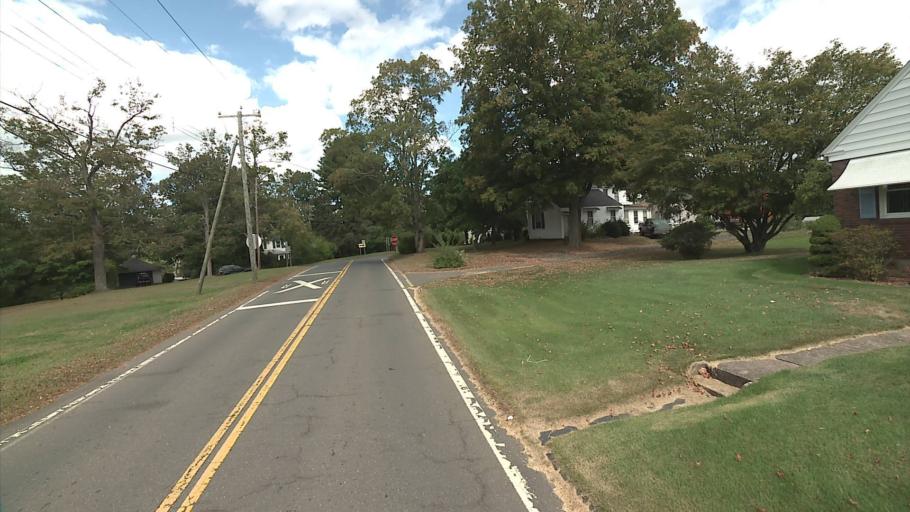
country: US
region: Connecticut
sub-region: Middlesex County
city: Middletown
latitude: 41.5444
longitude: -72.6826
